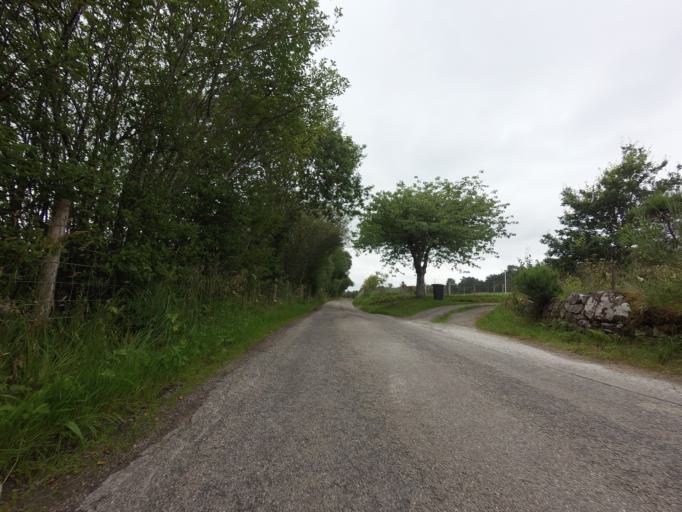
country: GB
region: Scotland
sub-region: Highland
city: Evanton
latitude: 57.9088
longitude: -4.3965
